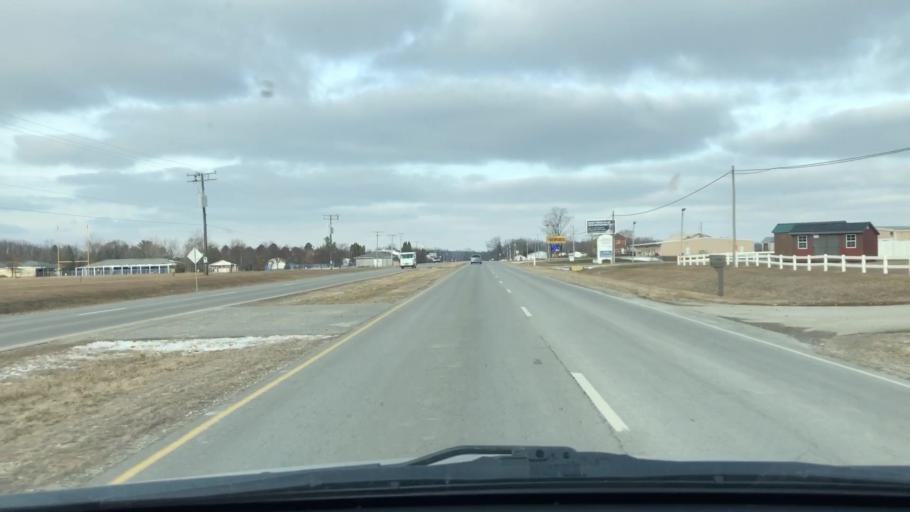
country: US
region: Indiana
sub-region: Steuben County
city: Angola
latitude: 41.6732
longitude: -85.0286
